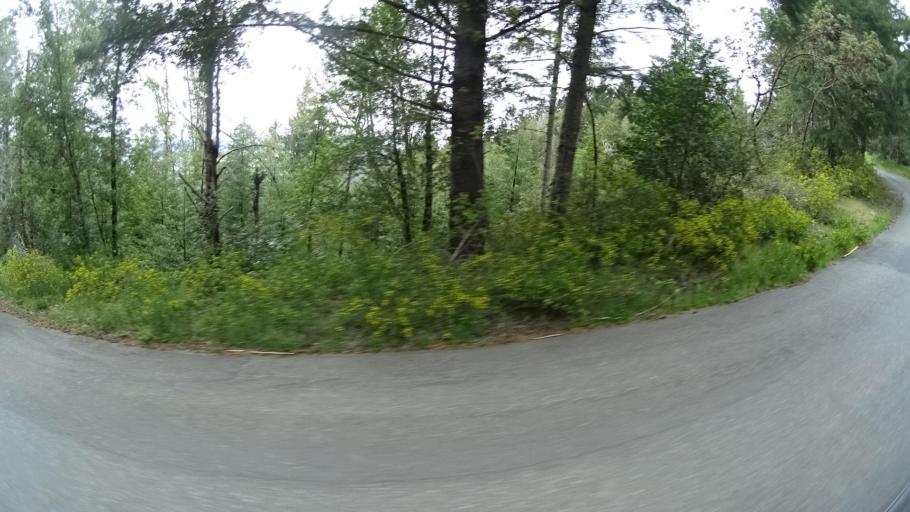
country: US
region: California
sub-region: Humboldt County
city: Redway
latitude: 40.2741
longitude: -123.7834
